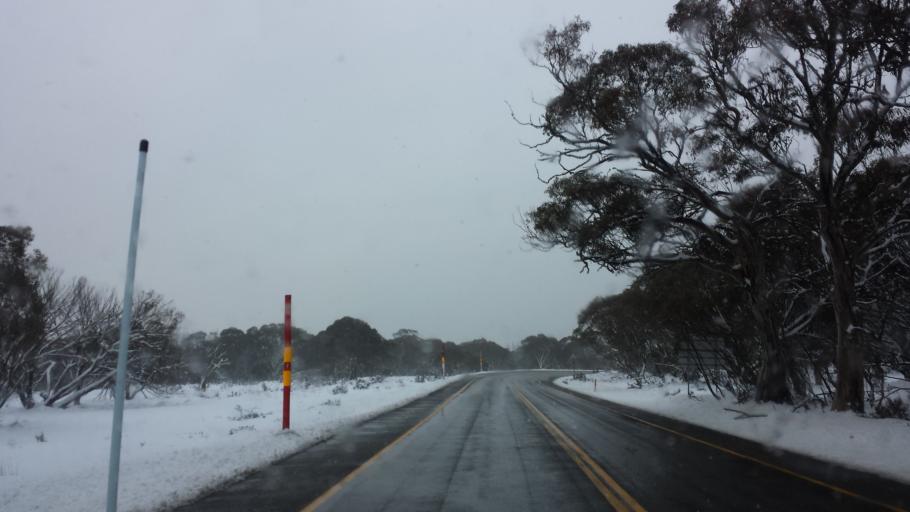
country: AU
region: Victoria
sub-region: Alpine
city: Mount Beauty
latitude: -37.0207
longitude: 147.2416
